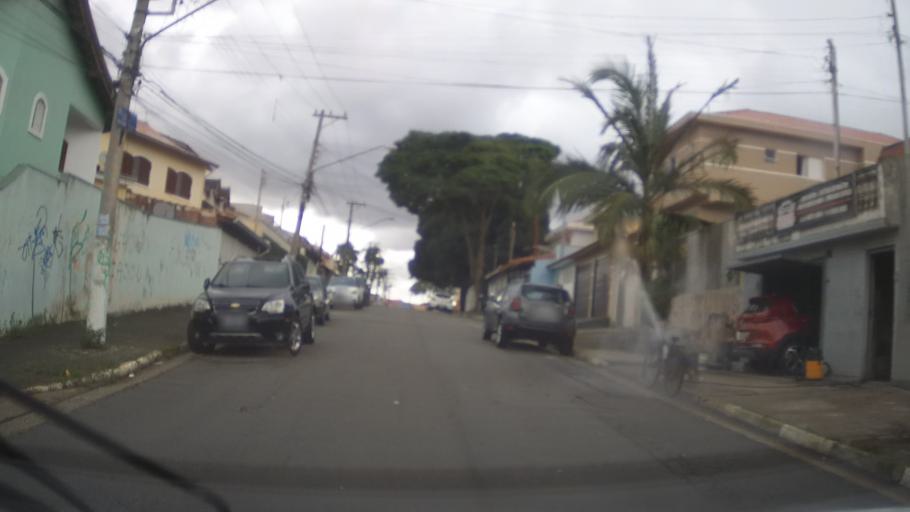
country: BR
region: Sao Paulo
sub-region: Guarulhos
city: Guarulhos
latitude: -23.4641
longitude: -46.5587
